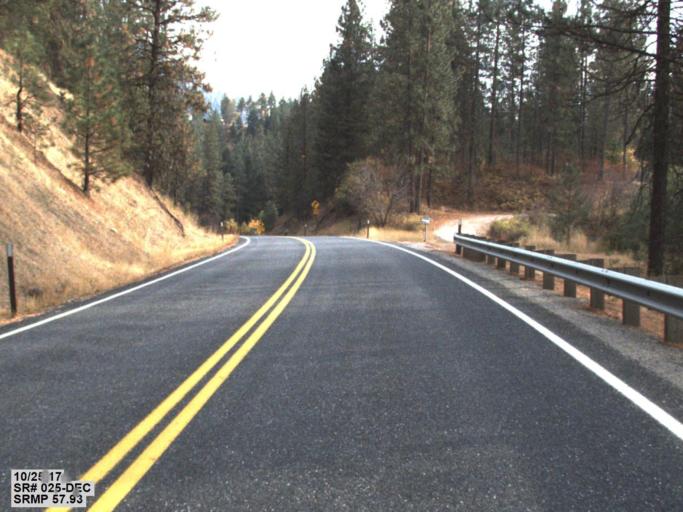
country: US
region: Washington
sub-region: Stevens County
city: Kettle Falls
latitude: 48.3094
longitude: -118.1480
